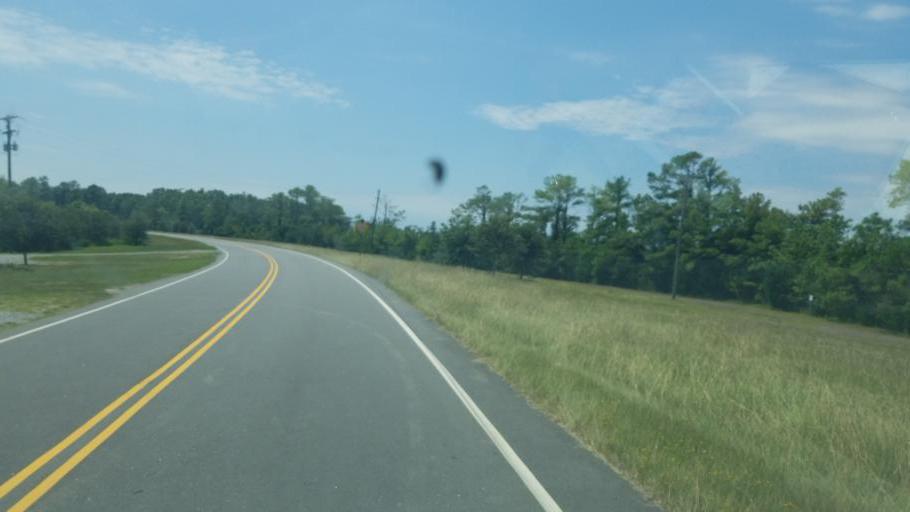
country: US
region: North Carolina
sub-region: Dare County
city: Manteo
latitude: 35.9096
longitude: -75.7734
